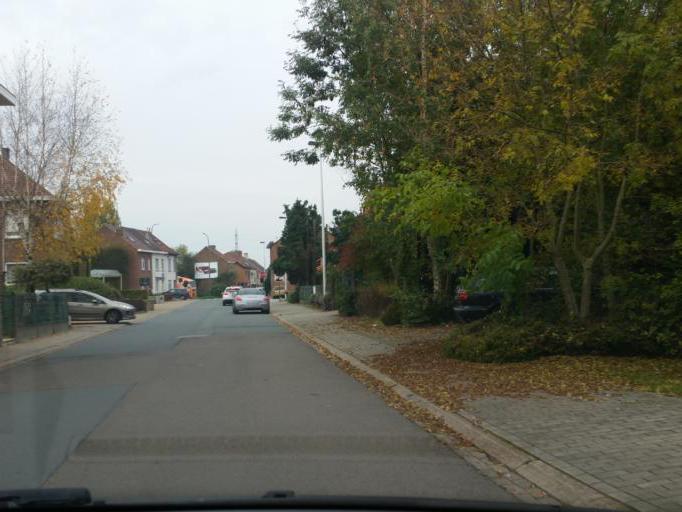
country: BE
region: Flanders
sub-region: Provincie Vlaams-Brabant
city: Halle
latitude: 50.7230
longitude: 4.2558
